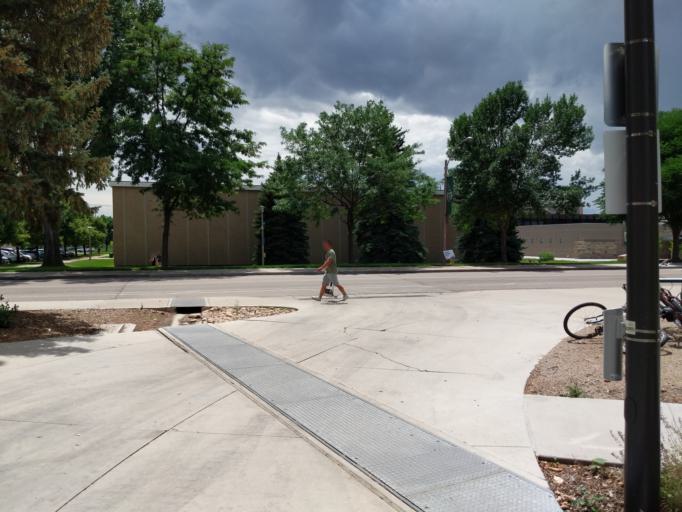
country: US
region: Colorado
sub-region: Larimer County
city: Fort Collins
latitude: 40.5766
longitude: -105.0913
